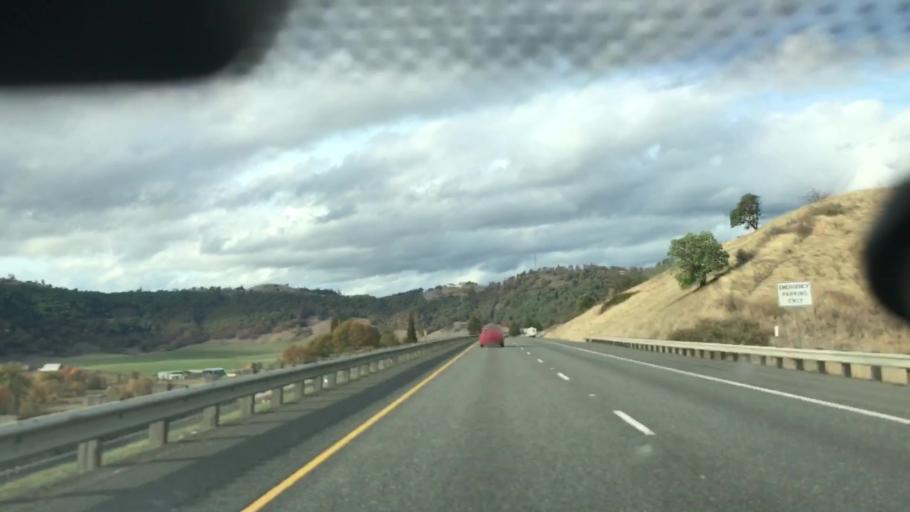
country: US
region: Oregon
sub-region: Douglas County
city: Winston
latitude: 43.0858
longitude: -123.3664
